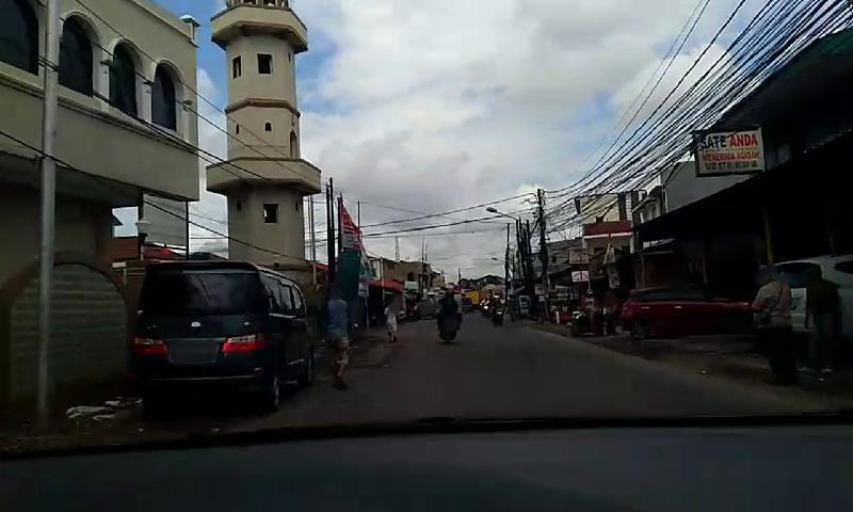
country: ID
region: West Java
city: Bekasi
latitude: -6.1980
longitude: 106.9875
